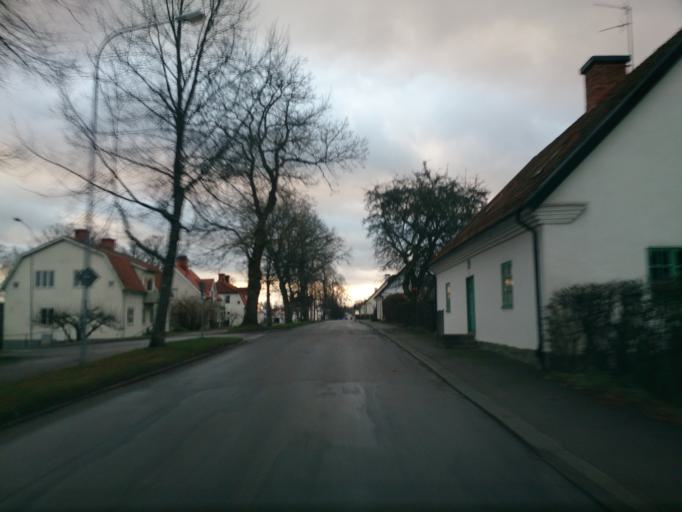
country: SE
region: OEstergoetland
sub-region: Atvidabergs Kommun
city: Atvidaberg
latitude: 58.2031
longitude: 15.9937
